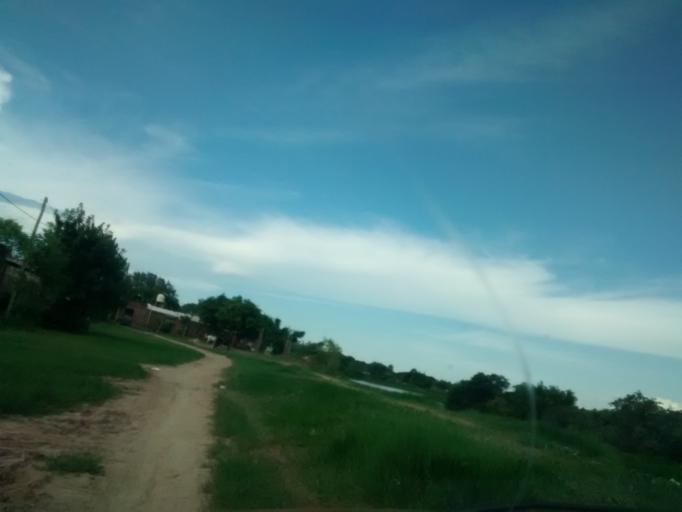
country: AR
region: Chaco
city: Resistencia
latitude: -27.4287
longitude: -58.9763
